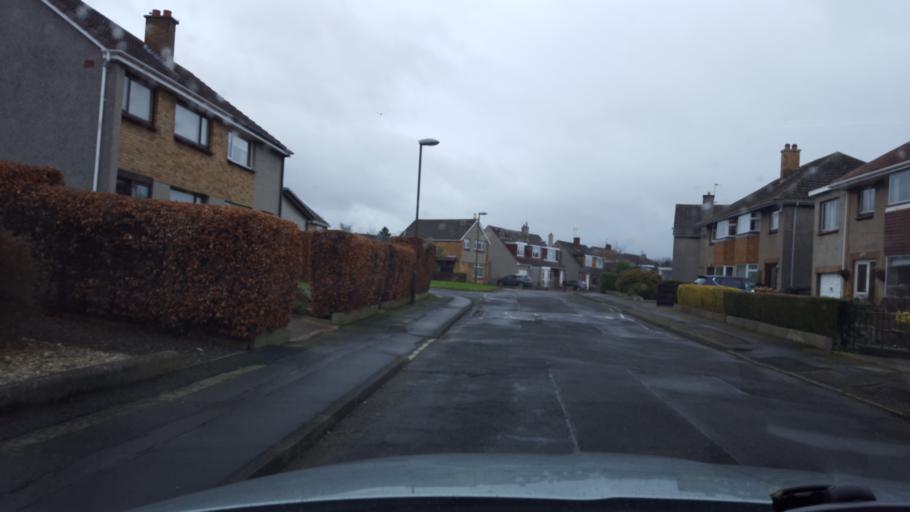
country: GB
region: Scotland
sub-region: Edinburgh
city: Currie
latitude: 55.9027
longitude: -3.2973
